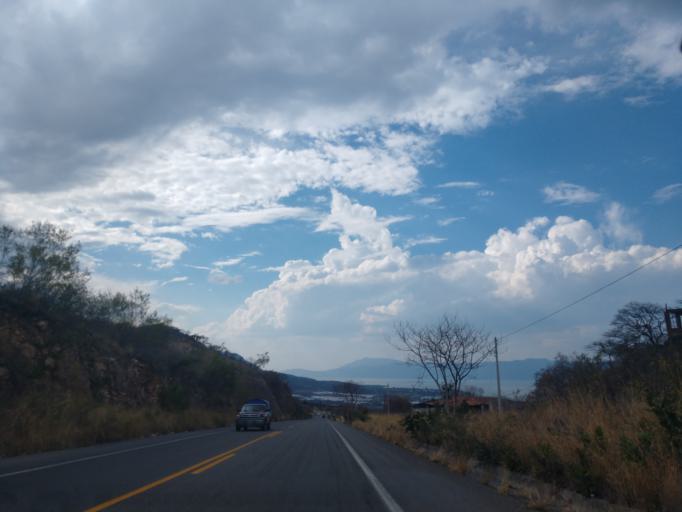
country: MX
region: Jalisco
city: La Manzanilla de la Paz
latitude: 20.1256
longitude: -103.1594
